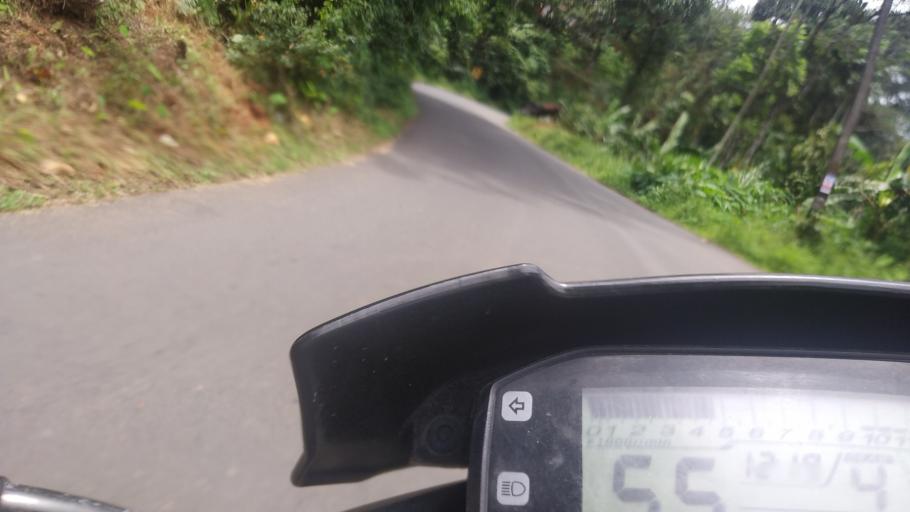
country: IN
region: Kerala
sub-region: Idukki
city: Munnar
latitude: 10.0223
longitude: 77.0015
